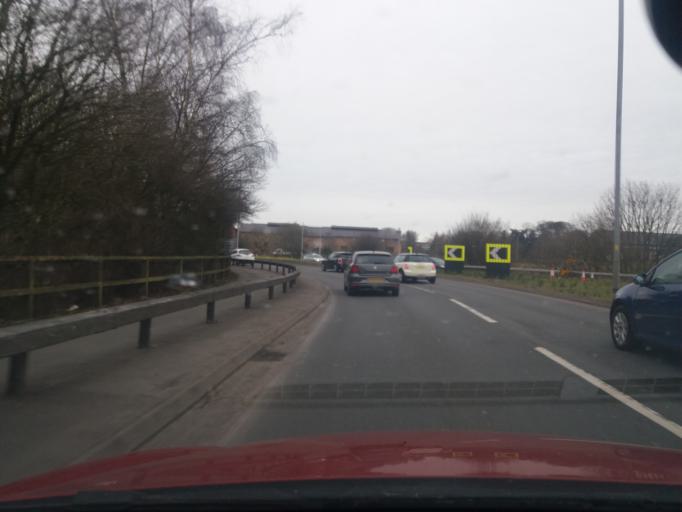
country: GB
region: England
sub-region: Lancashire
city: Chorley
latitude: 53.6697
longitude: -2.6266
